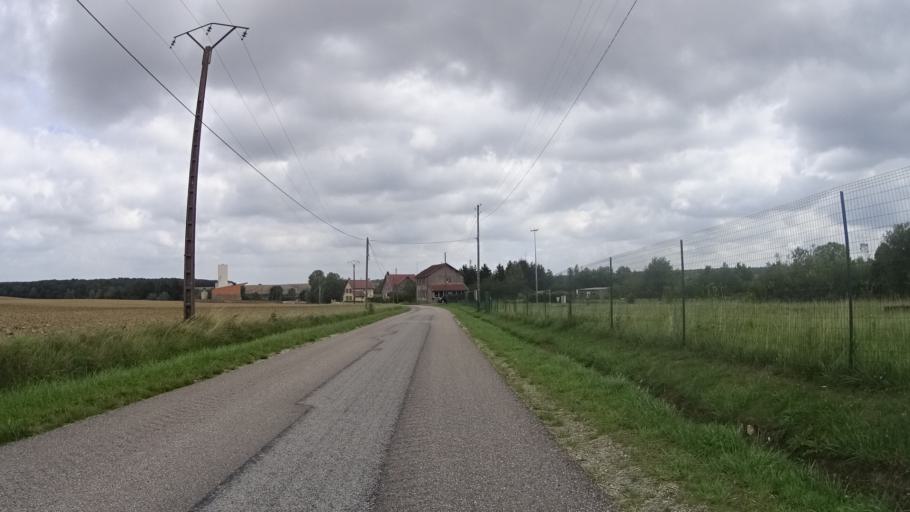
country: FR
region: Lorraine
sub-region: Departement de la Meuse
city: Ligny-en-Barrois
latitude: 48.7492
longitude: 5.4029
